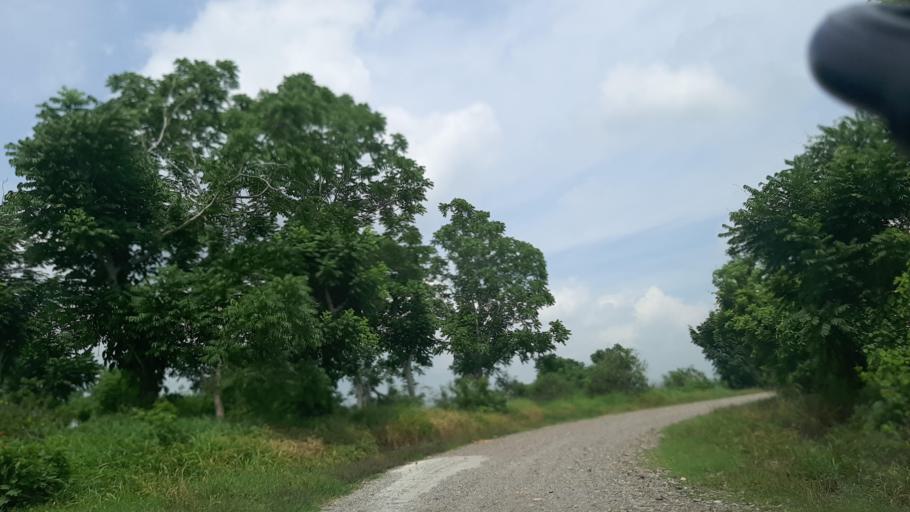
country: MX
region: Veracruz
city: Gutierrez Zamora
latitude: 20.4479
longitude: -97.1764
